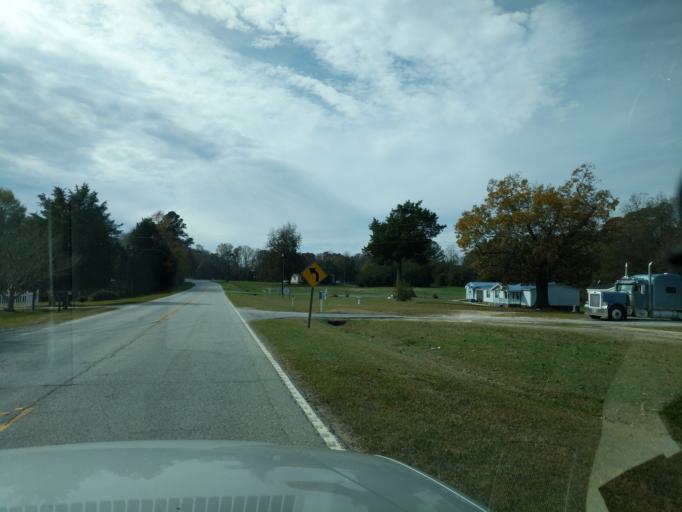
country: US
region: South Carolina
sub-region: Laurens County
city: Watts Mills
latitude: 34.6013
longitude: -81.9887
